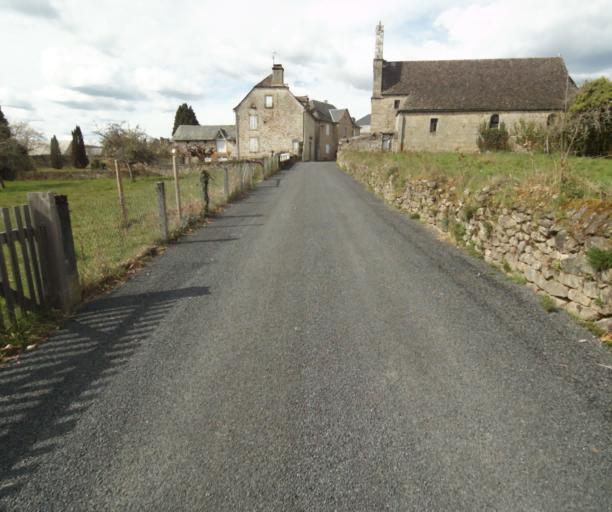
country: FR
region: Limousin
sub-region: Departement de la Correze
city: Argentat
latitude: 45.1849
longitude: 1.9517
